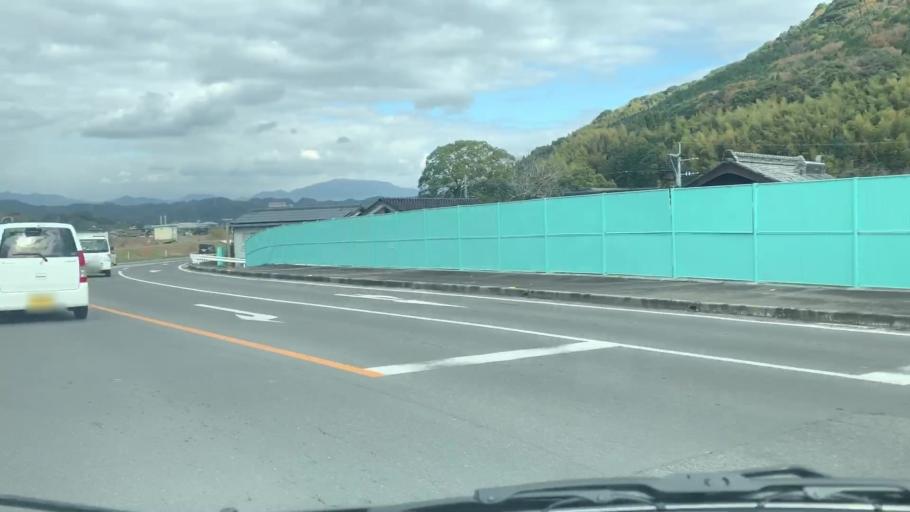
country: JP
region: Saga Prefecture
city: Takeocho-takeo
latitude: 33.2019
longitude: 130.0536
